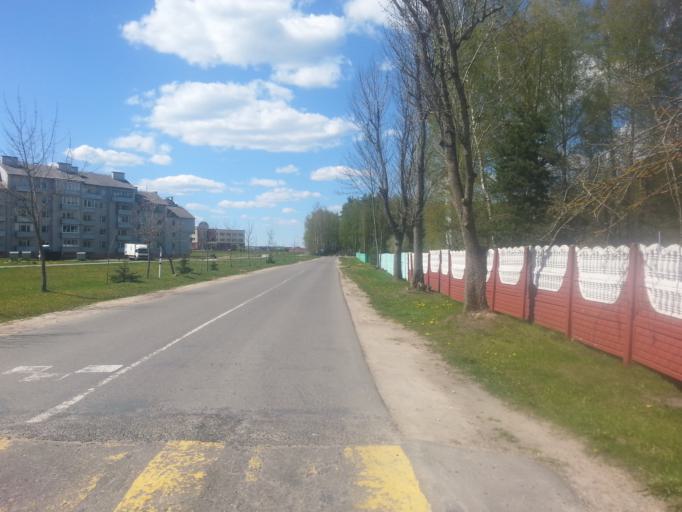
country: BY
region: Minsk
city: Narach
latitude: 54.9171
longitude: 26.7006
